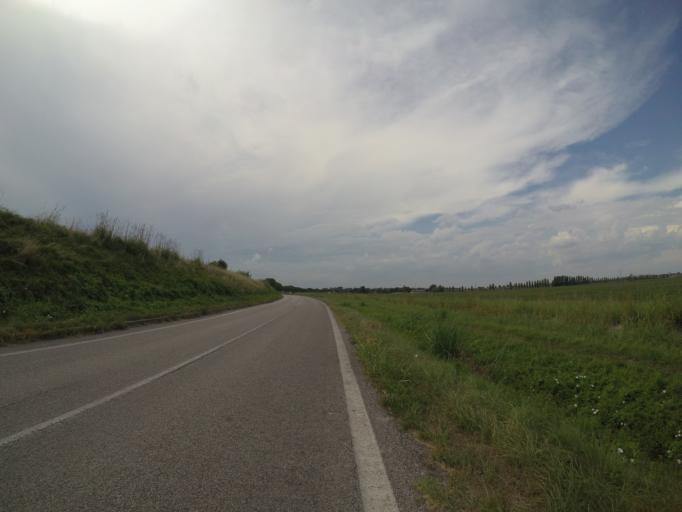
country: IT
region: Friuli Venezia Giulia
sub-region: Provincia di Udine
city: Pertegada
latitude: 45.6799
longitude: 13.0642
